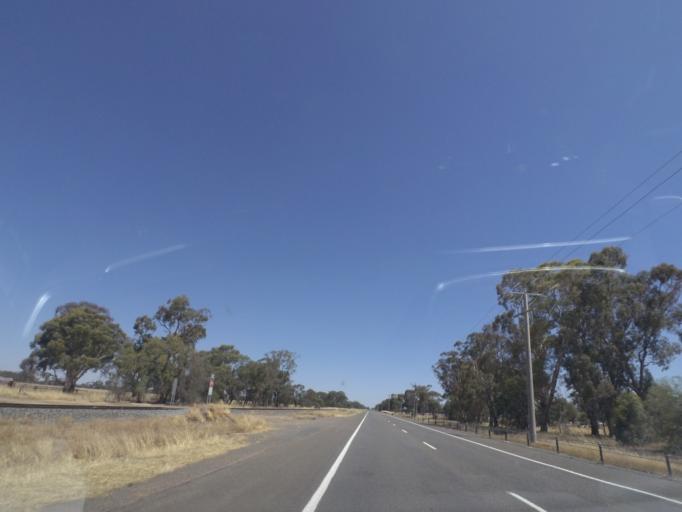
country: AU
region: Victoria
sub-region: Greater Shepparton
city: Shepparton
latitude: -36.2436
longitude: 145.4319
